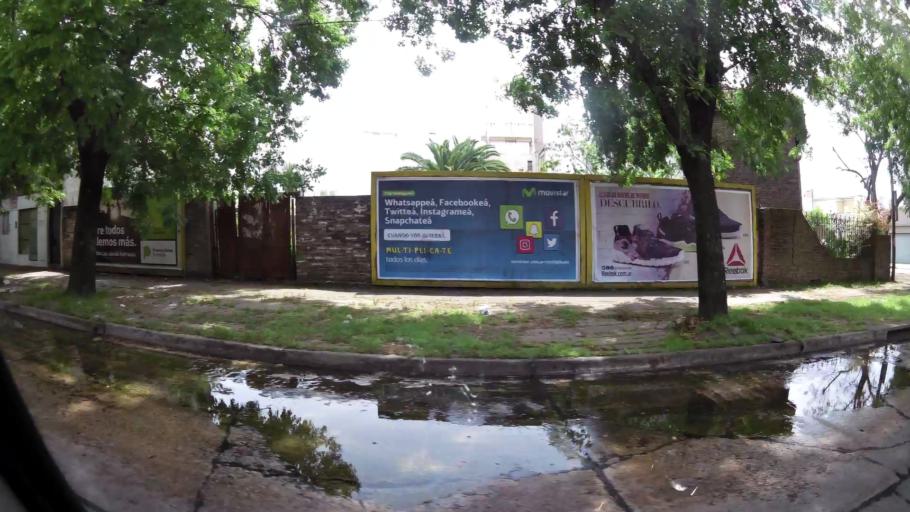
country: AR
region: Buenos Aires
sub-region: Partido de La Plata
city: La Plata
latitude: -34.9458
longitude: -57.9566
